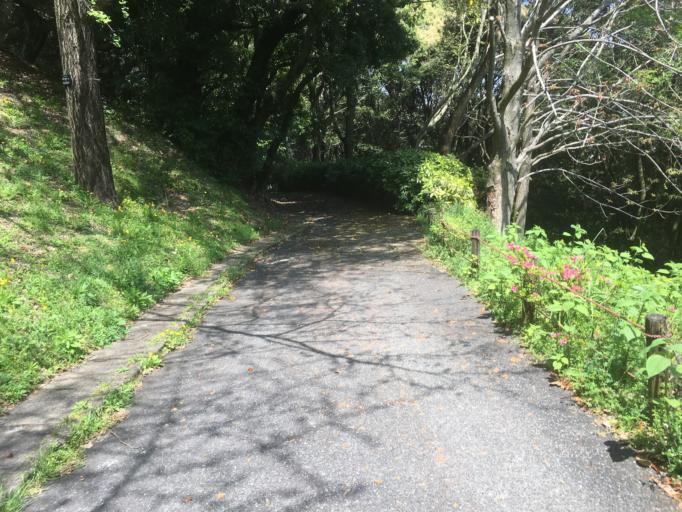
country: JP
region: Fukuoka
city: Fukuoka-shi
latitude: 33.5711
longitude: 130.3924
